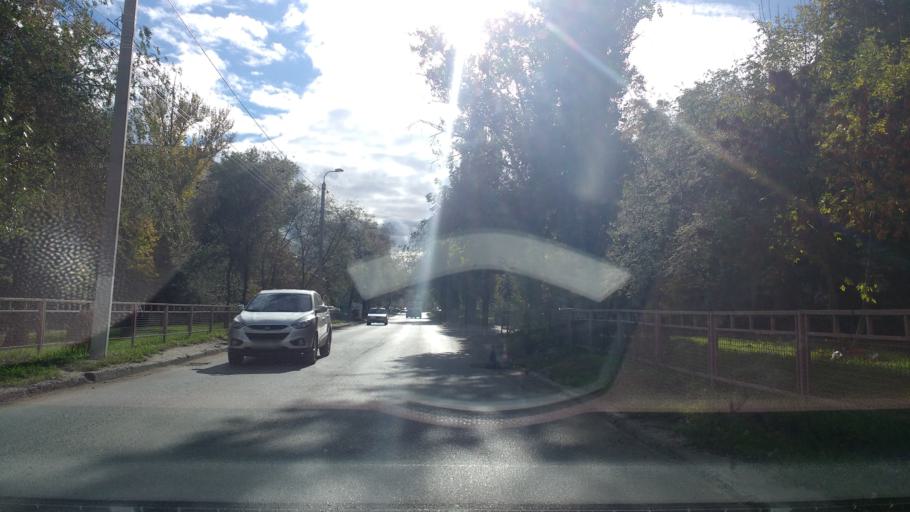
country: RU
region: Volgograd
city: Krasnoslobodsk
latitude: 48.7727
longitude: 44.5592
